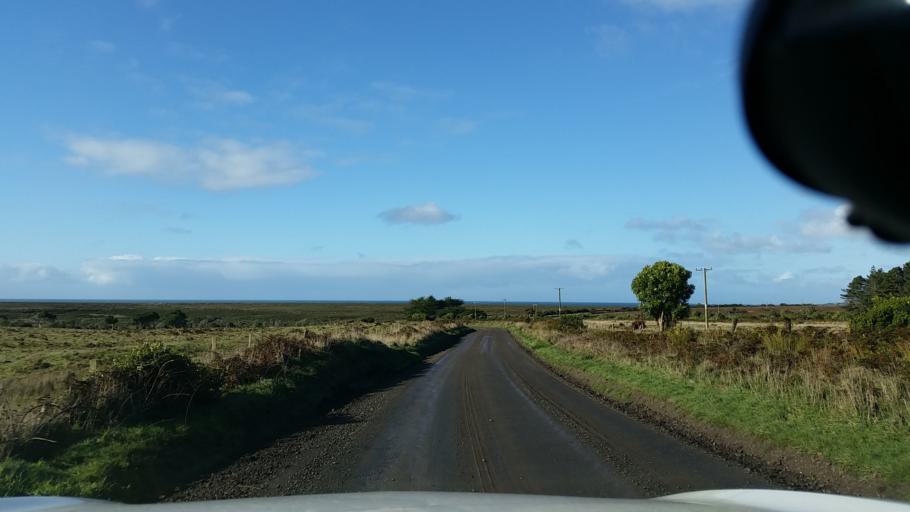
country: NZ
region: Chatham Islands
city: Waitangi
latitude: -43.9929
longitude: -176.4258
